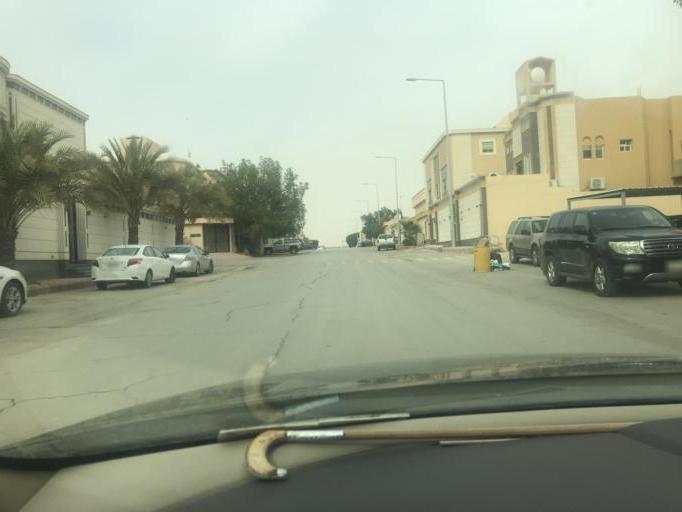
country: SA
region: Ar Riyad
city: Riyadh
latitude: 24.7548
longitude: 46.7645
